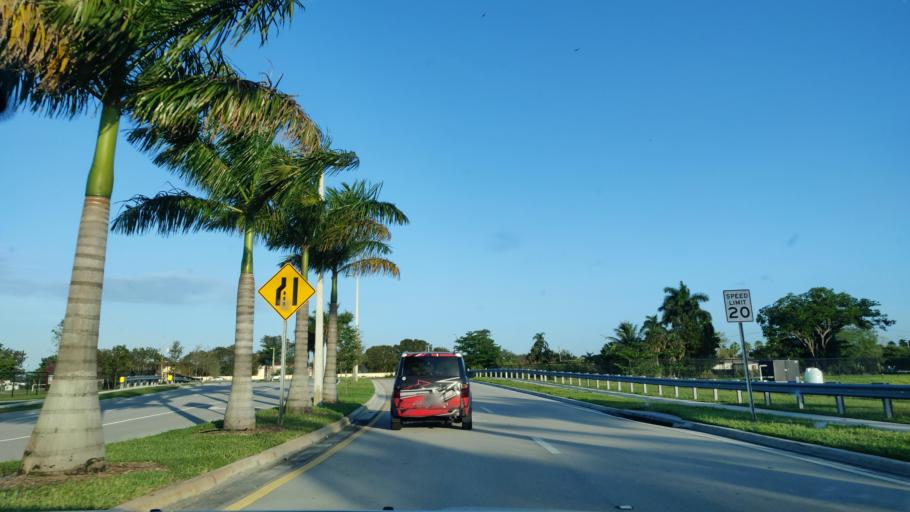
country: US
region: Florida
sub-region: Miami-Dade County
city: Westview
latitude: 25.8800
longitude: -80.2370
